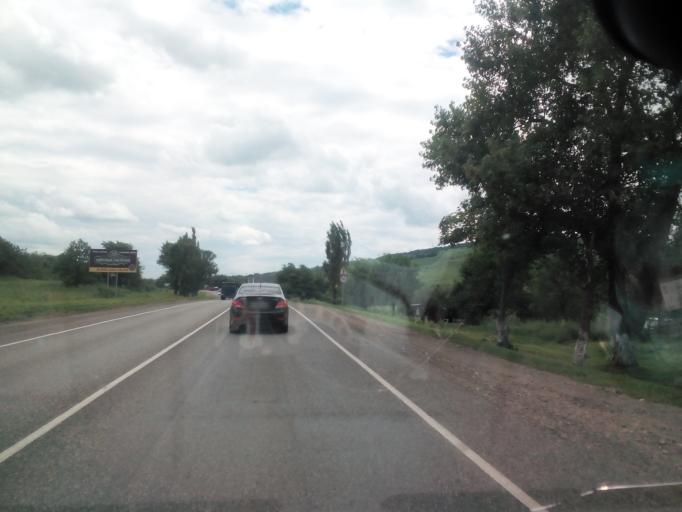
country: RU
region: Stavropol'skiy
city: Tatarka
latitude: 44.8799
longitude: 41.9272
